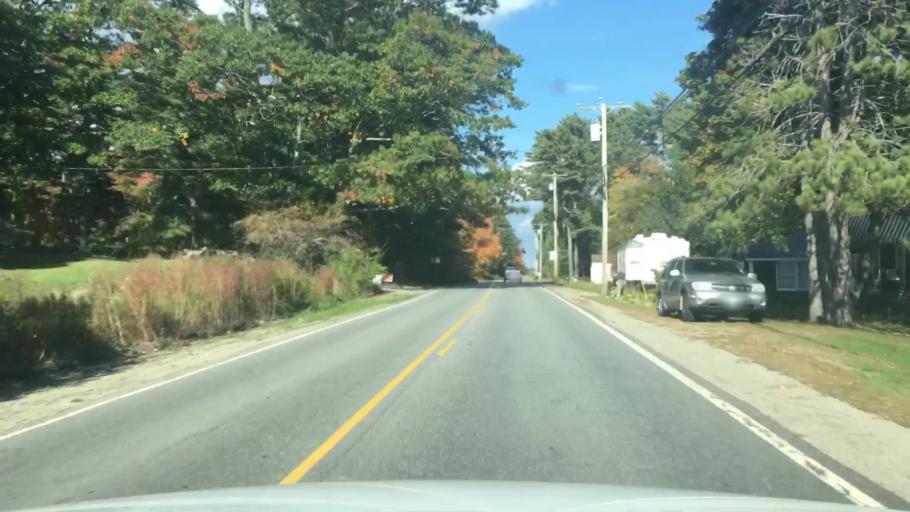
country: US
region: Maine
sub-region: Knox County
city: Warren
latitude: 44.1286
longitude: -69.2396
